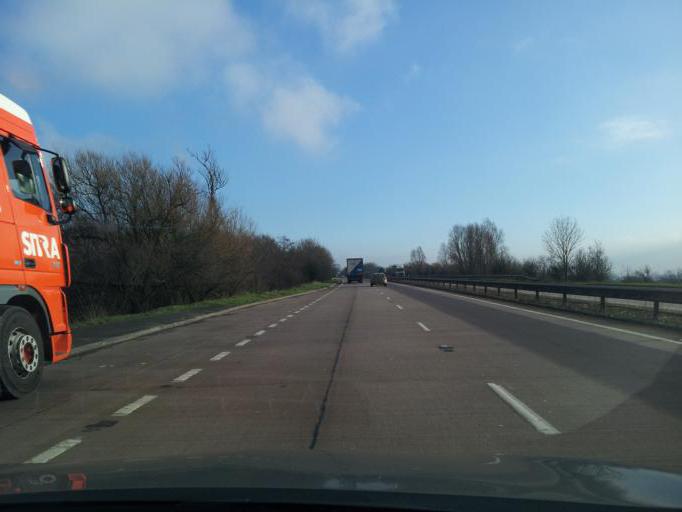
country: GB
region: England
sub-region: Staffordshire
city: Cheadle
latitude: 52.9468
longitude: -2.0103
